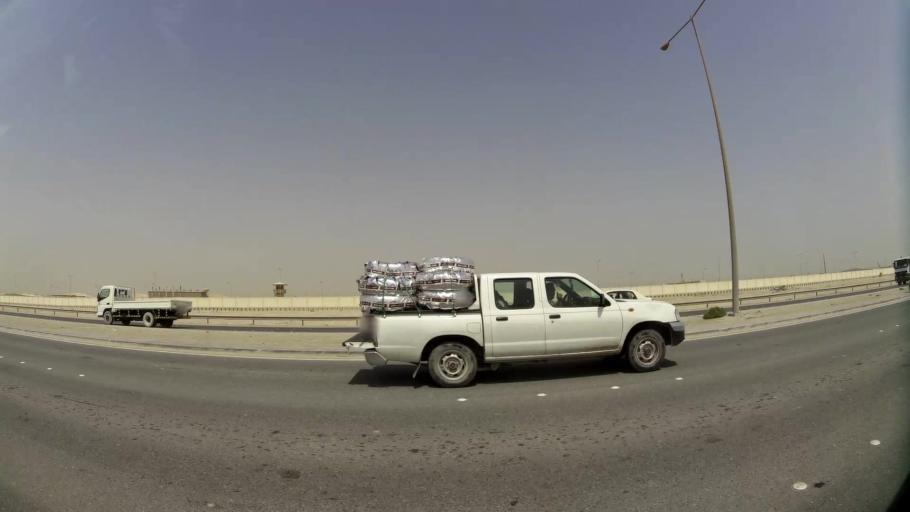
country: QA
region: Baladiyat ar Rayyan
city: Ar Rayyan
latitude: 25.1819
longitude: 51.4207
